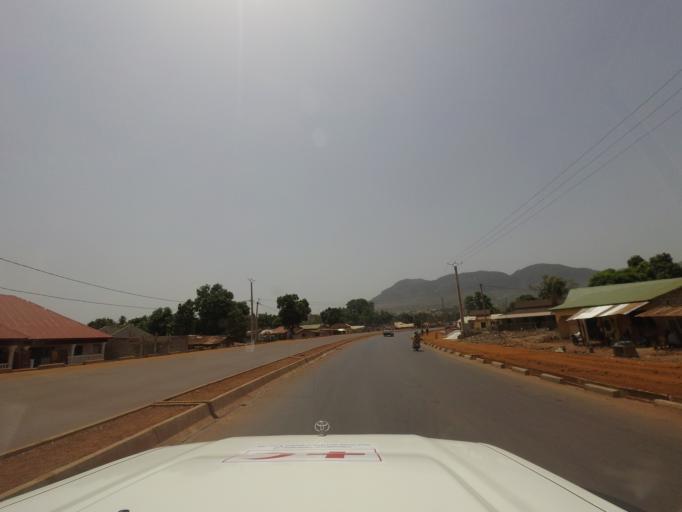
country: GN
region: Kindia
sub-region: Coyah
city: Coyah
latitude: 9.7234
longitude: -13.4153
